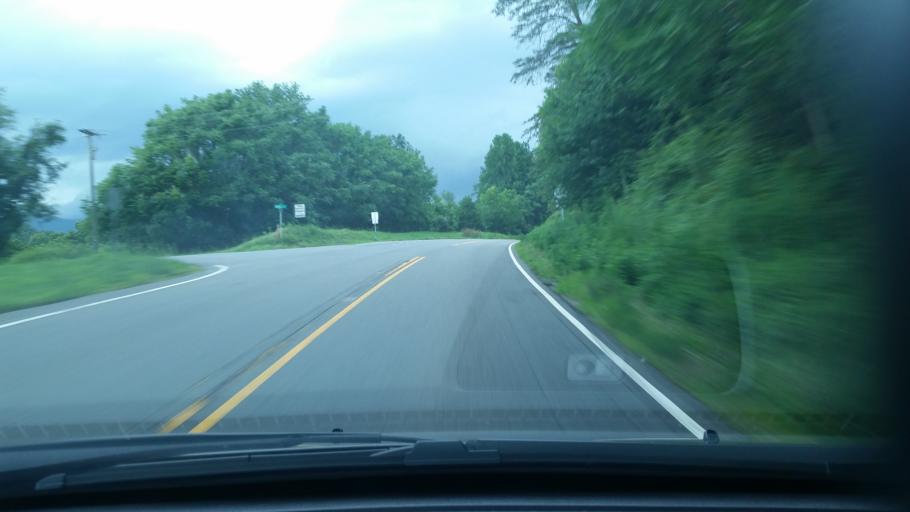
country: US
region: Virginia
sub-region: Nelson County
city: Nellysford
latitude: 37.8696
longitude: -78.8203
